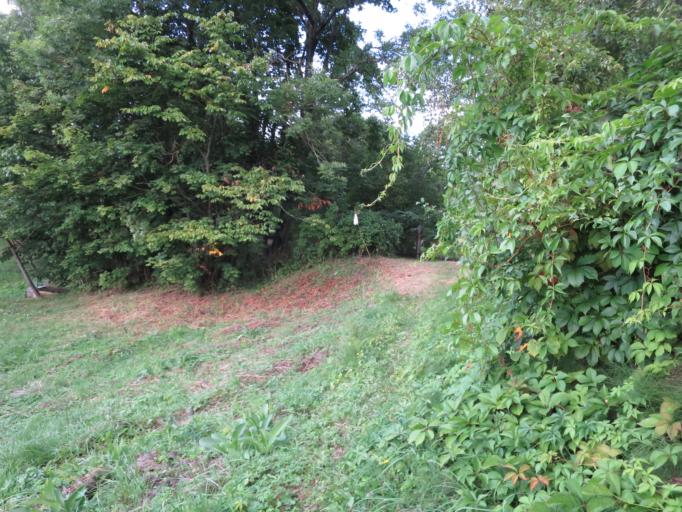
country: LV
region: Malpils
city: Malpils
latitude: 56.8885
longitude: 25.1809
